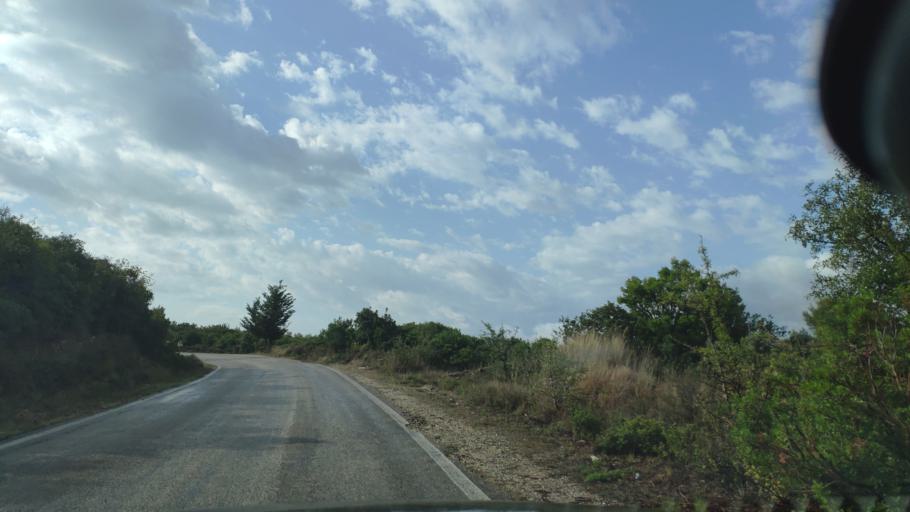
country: GR
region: West Greece
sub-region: Nomos Aitolias kai Akarnanias
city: Sardinia
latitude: 38.8794
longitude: 21.2473
